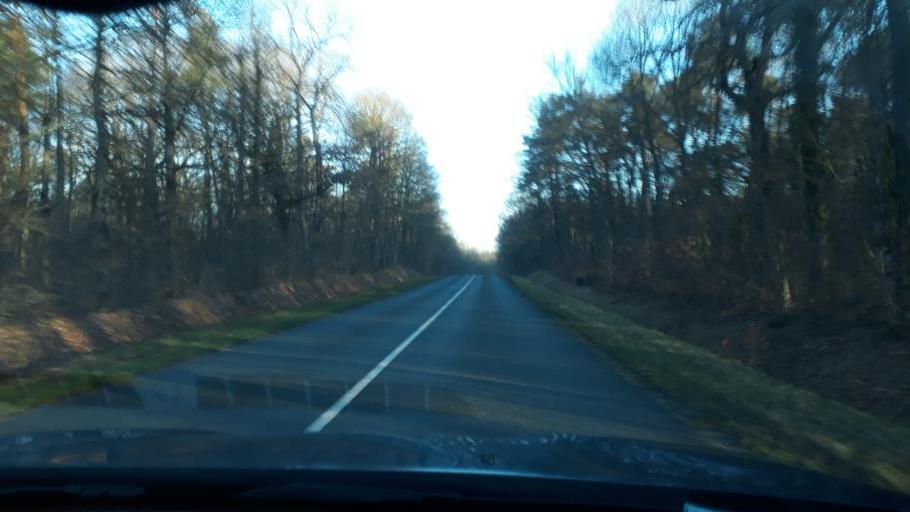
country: FR
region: Centre
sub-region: Departement du Loiret
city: Neuville-aux-Bois
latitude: 48.0360
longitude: 2.0511
